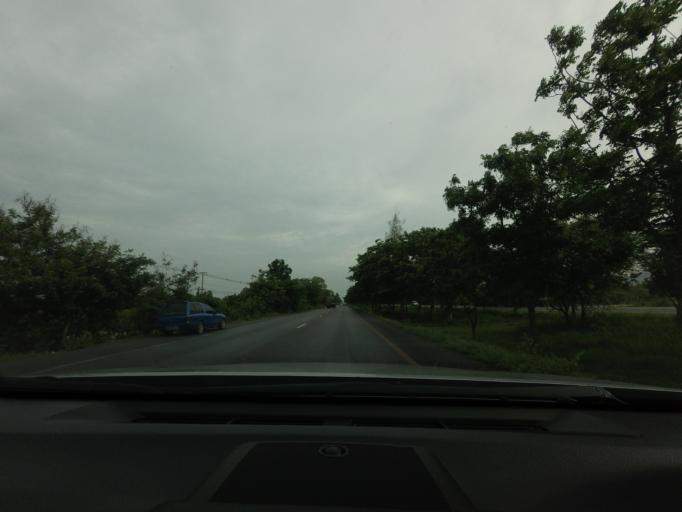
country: TH
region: Phetchaburi
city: Cha-am
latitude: 12.7738
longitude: 99.9364
